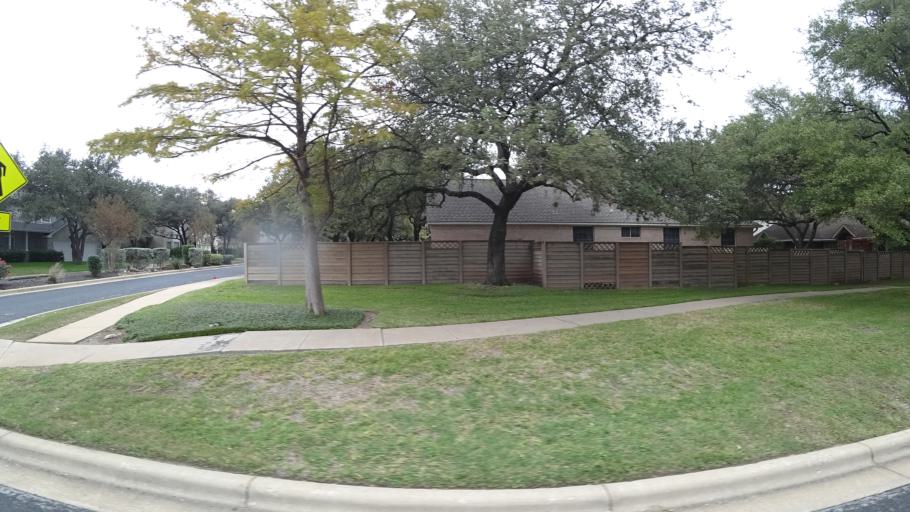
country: US
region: Texas
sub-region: Williamson County
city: Anderson Mill
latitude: 30.4407
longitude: -97.8253
